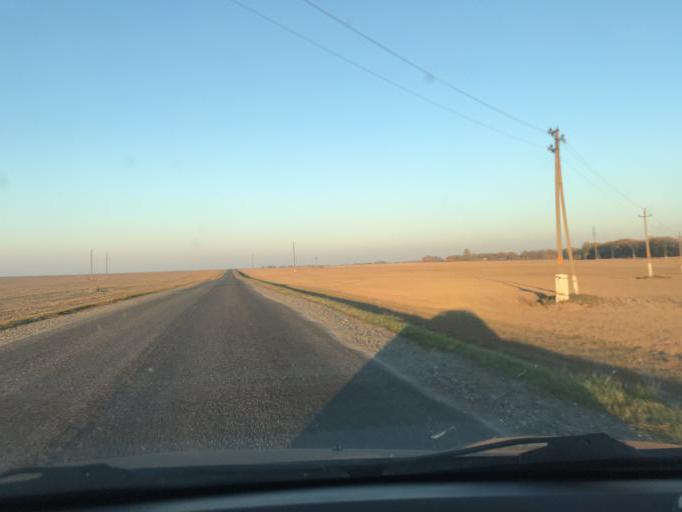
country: BY
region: Gomel
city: Brahin
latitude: 51.8120
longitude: 30.2874
